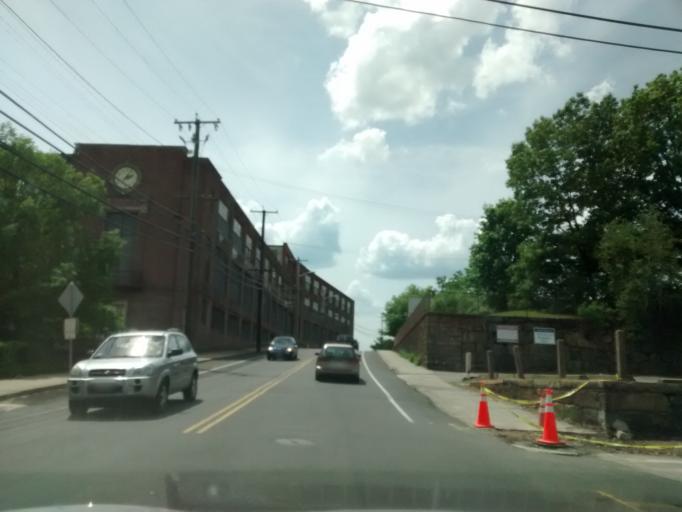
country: US
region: Massachusetts
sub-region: Worcester County
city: Whitinsville
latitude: 42.1103
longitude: -71.6685
